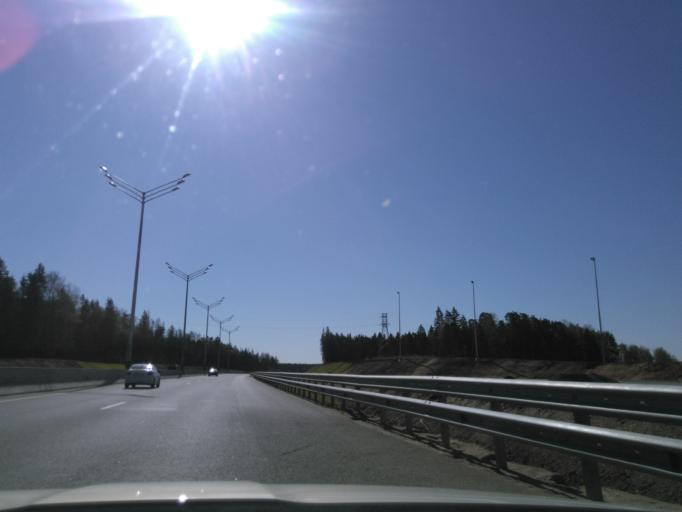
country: RU
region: Moskovskaya
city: Radumlya
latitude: 56.0964
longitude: 37.1846
